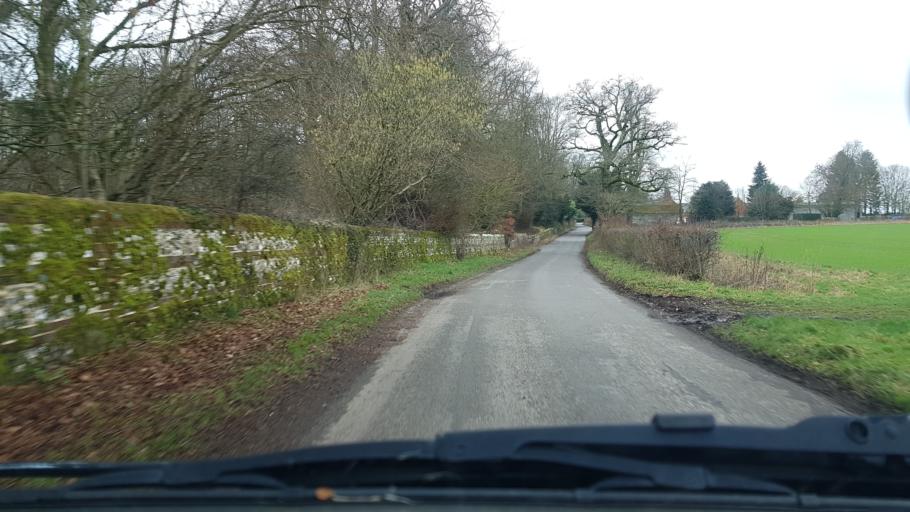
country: GB
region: England
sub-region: Wiltshire
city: Shalbourne
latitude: 51.3265
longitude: -1.5558
